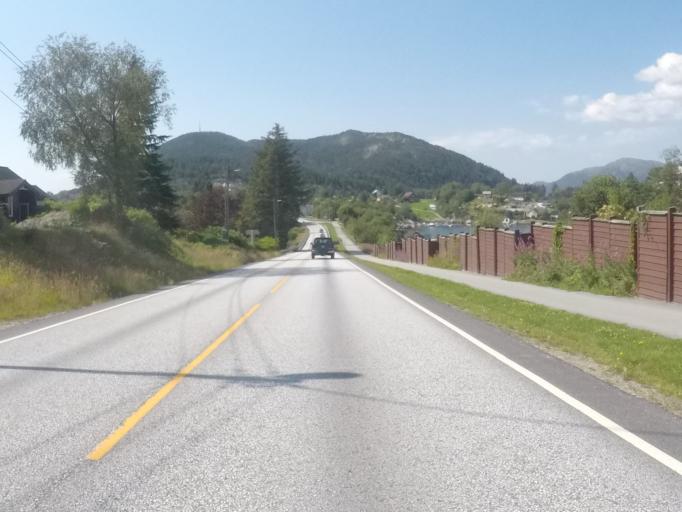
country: NO
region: Sogn og Fjordane
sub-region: Flora
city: Floro
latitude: 61.6022
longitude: 5.1449
